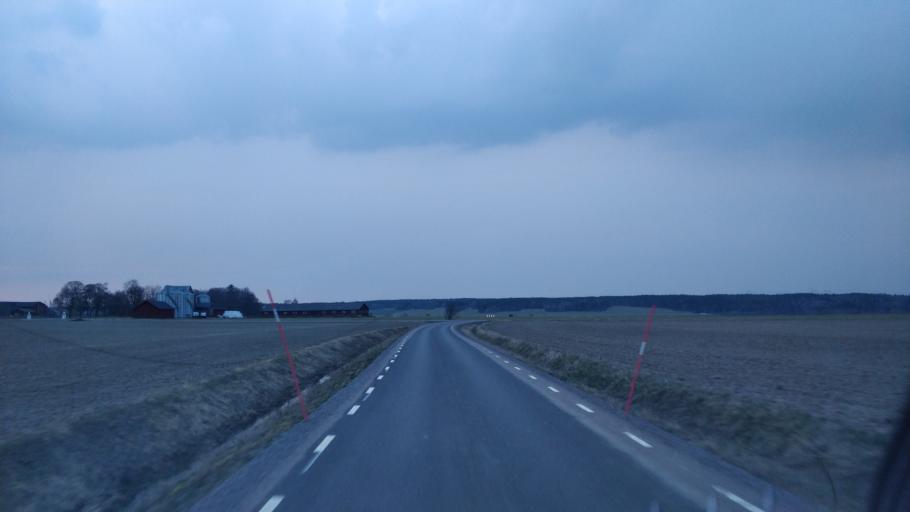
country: SE
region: Uppsala
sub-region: Enkopings Kommun
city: Orsundsbro
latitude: 59.7296
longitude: 17.2127
